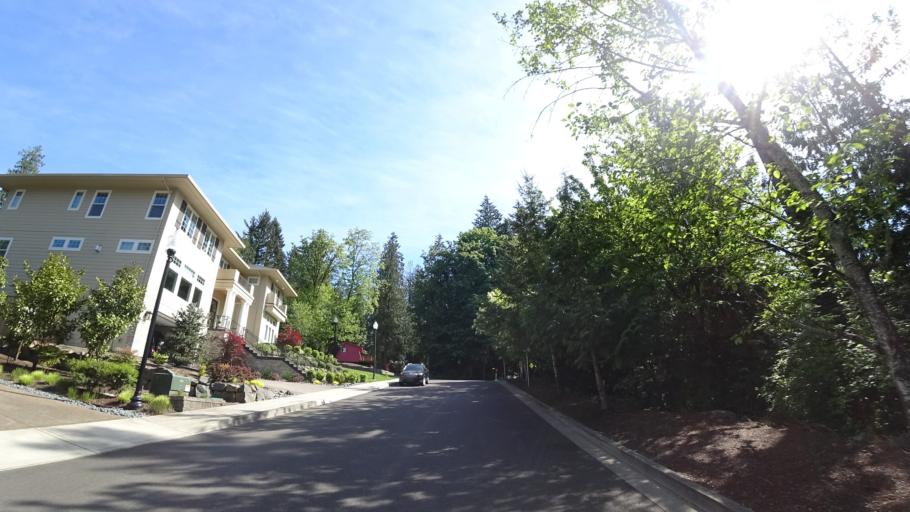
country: US
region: Oregon
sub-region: Washington County
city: West Slope
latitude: 45.4967
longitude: -122.7430
